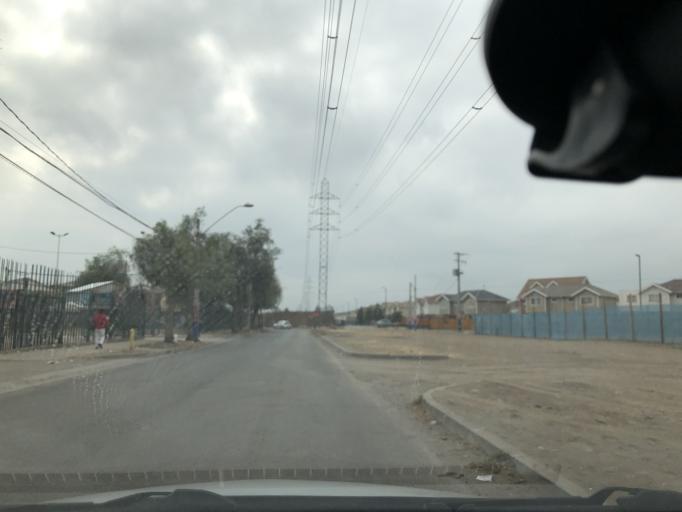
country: CL
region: Santiago Metropolitan
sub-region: Provincia de Cordillera
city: Puente Alto
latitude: -33.5944
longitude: -70.6010
